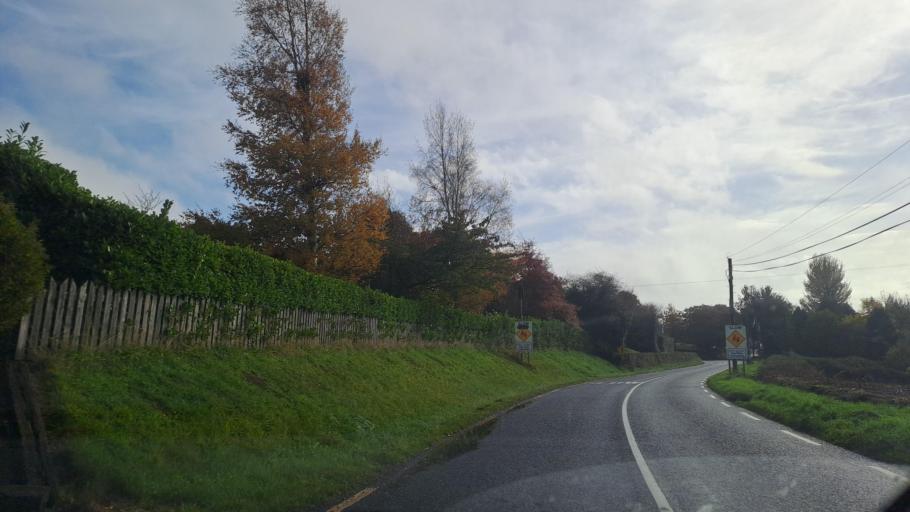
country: IE
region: Ulster
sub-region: County Monaghan
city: Carrickmacross
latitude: 53.9232
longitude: -6.7131
